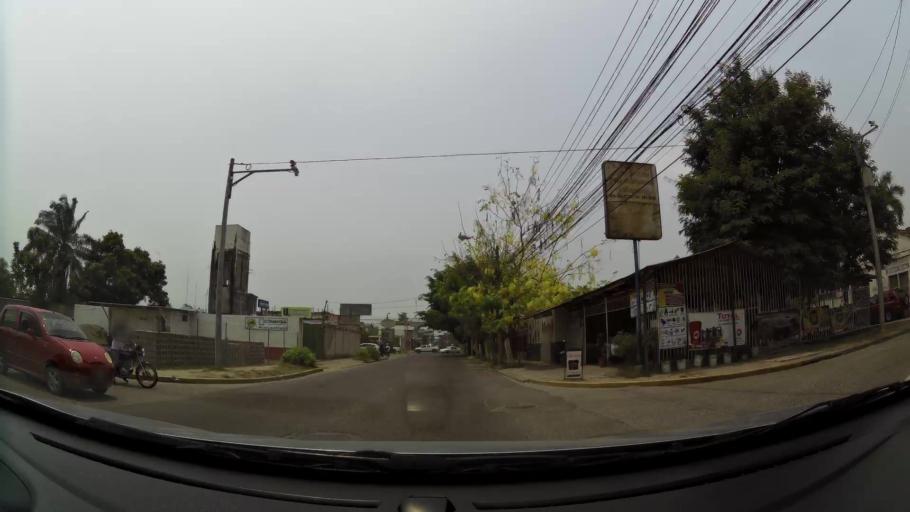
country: HN
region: Yoro
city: El Progreso
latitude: 15.3988
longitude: -87.8093
